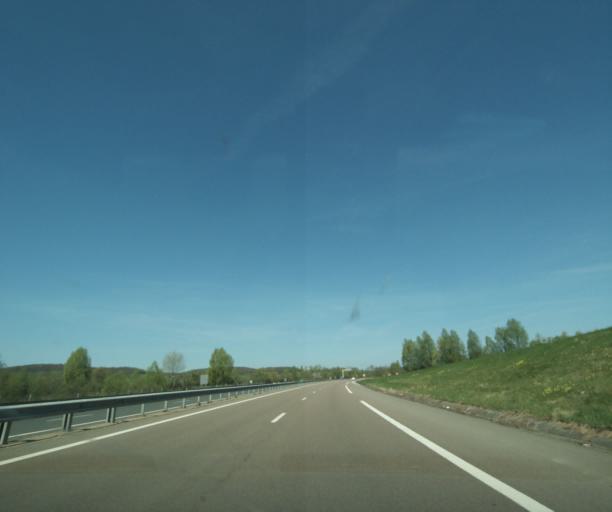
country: FR
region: Bourgogne
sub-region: Departement de la Nievre
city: Varennes-Vauzelles
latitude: 47.0495
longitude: 3.1316
